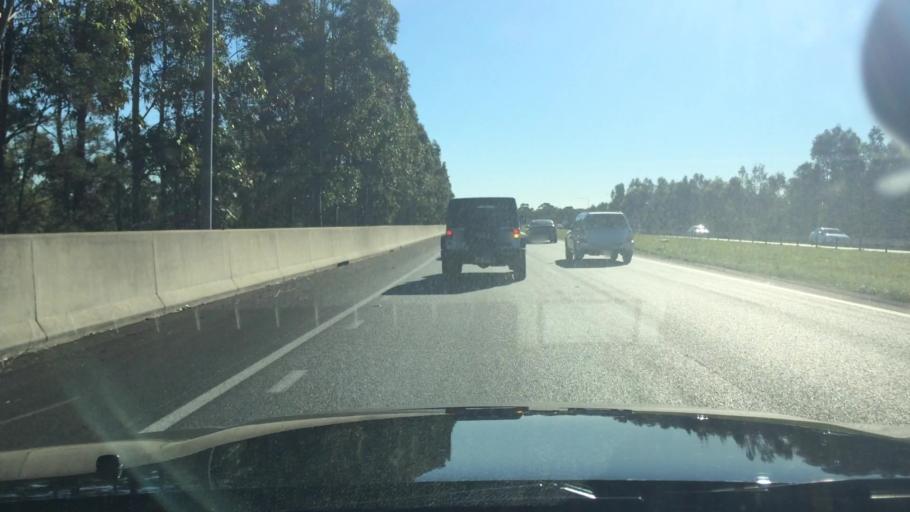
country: AU
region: New South Wales
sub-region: Blacktown
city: Doonside
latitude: -33.7884
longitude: 150.8567
